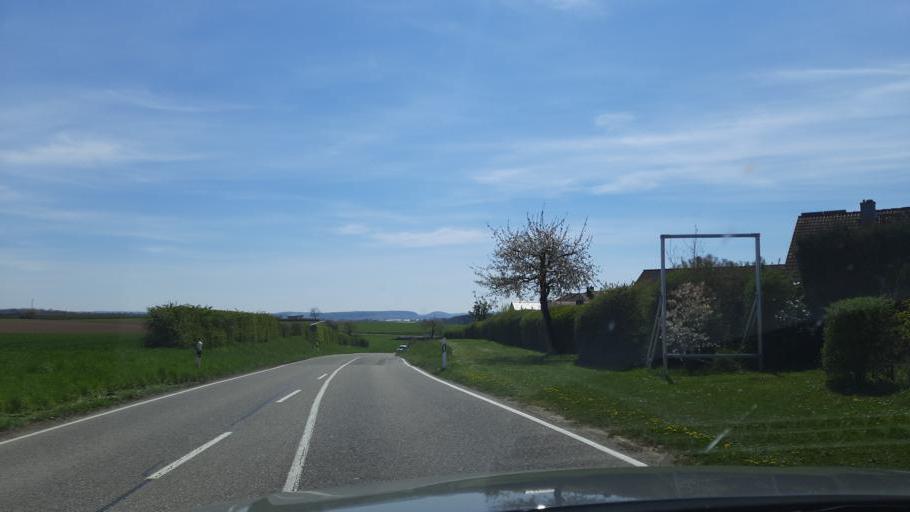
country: DE
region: Baden-Wuerttemberg
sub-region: Regierungsbezirk Stuttgart
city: Neuenstadt am Kocher
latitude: 49.2298
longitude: 9.3835
